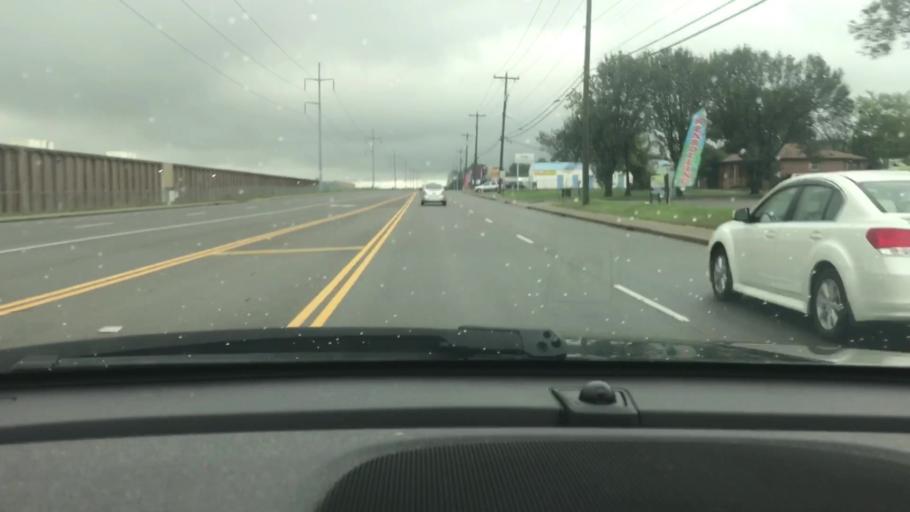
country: US
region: Tennessee
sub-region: Rutherford County
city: La Vergne
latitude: 36.0046
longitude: -86.5954
